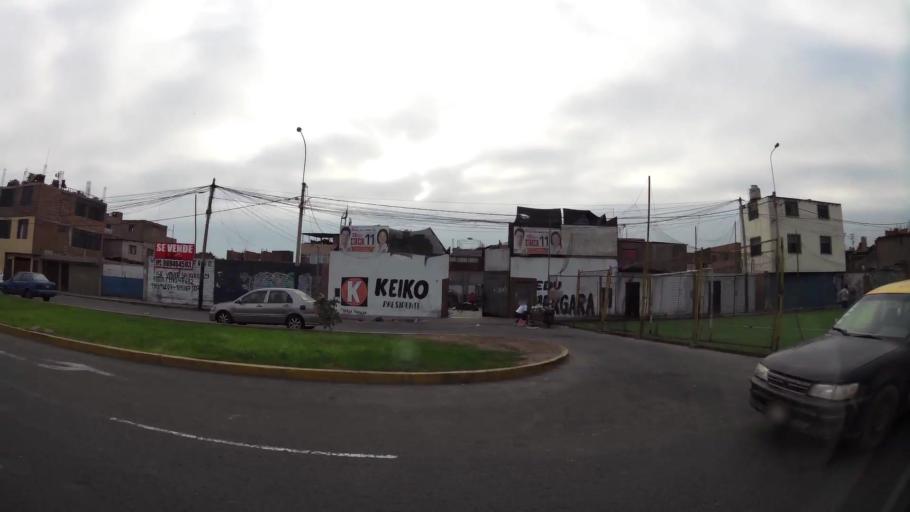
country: PE
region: Lima
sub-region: Lima
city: Surco
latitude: -12.1464
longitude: -77.0104
